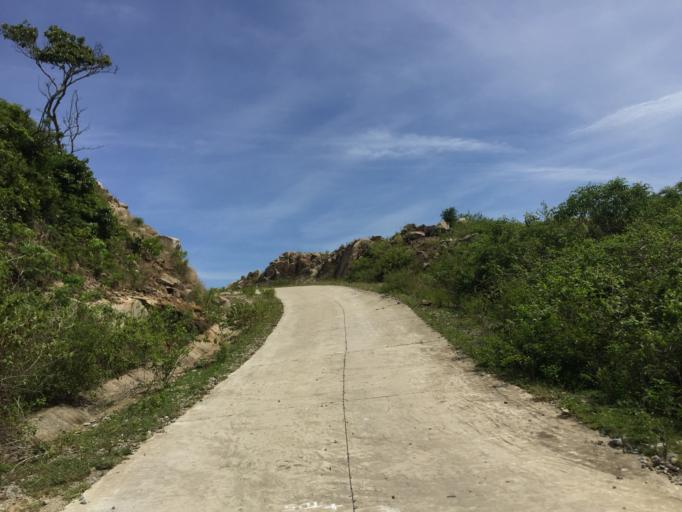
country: VN
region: Quang Nam
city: Hoi An
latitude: 15.9641
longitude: 108.5101
